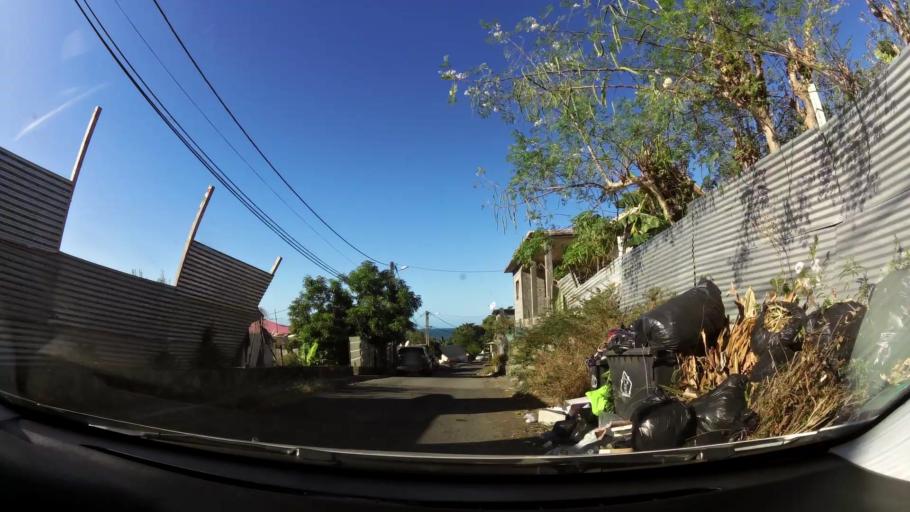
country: YT
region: Mamoudzou
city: Mamoudzou
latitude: -12.7547
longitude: 45.2305
